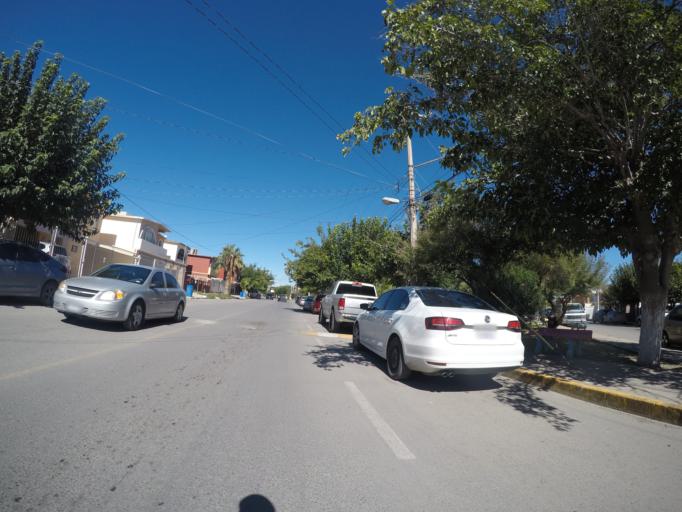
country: MX
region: Chihuahua
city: Ciudad Juarez
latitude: 31.7175
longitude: -106.4192
